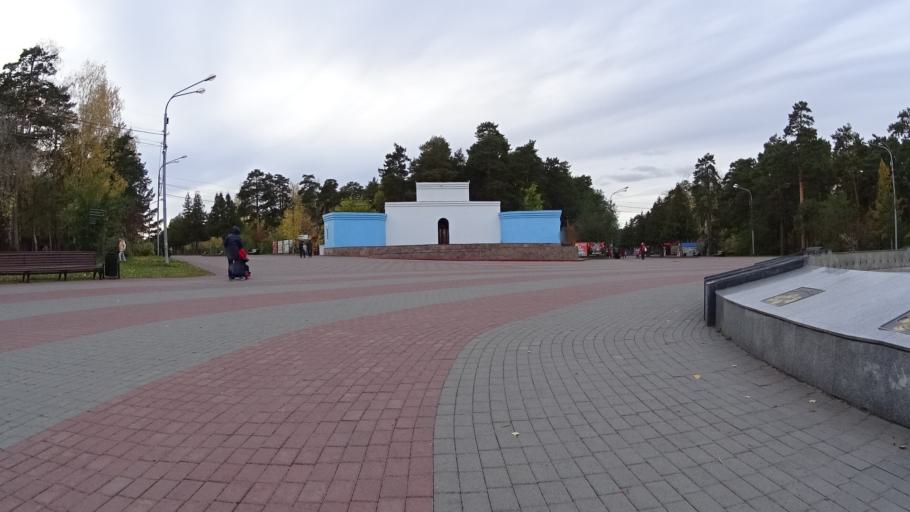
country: RU
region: Chelyabinsk
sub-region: Gorod Chelyabinsk
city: Chelyabinsk
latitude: 55.1633
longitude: 61.3719
